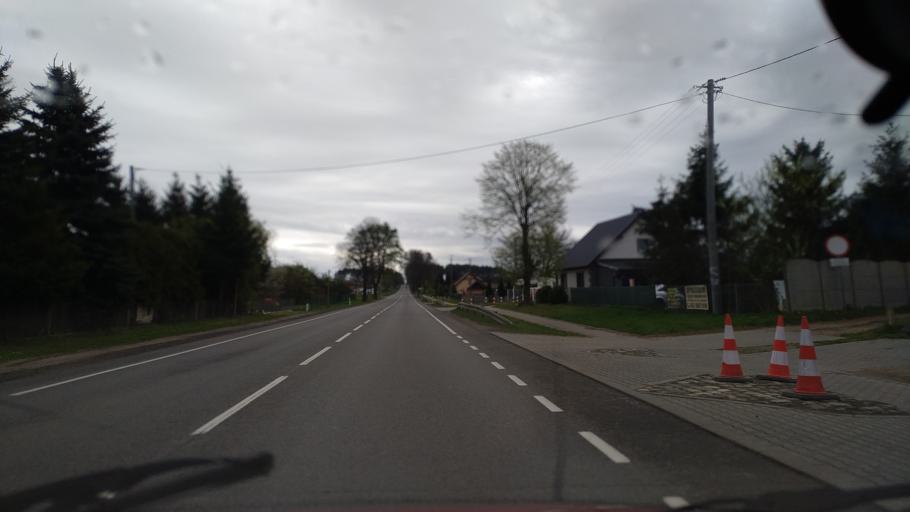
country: PL
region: Pomeranian Voivodeship
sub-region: Powiat starogardzki
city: Zblewo
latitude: 53.9326
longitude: 18.3443
